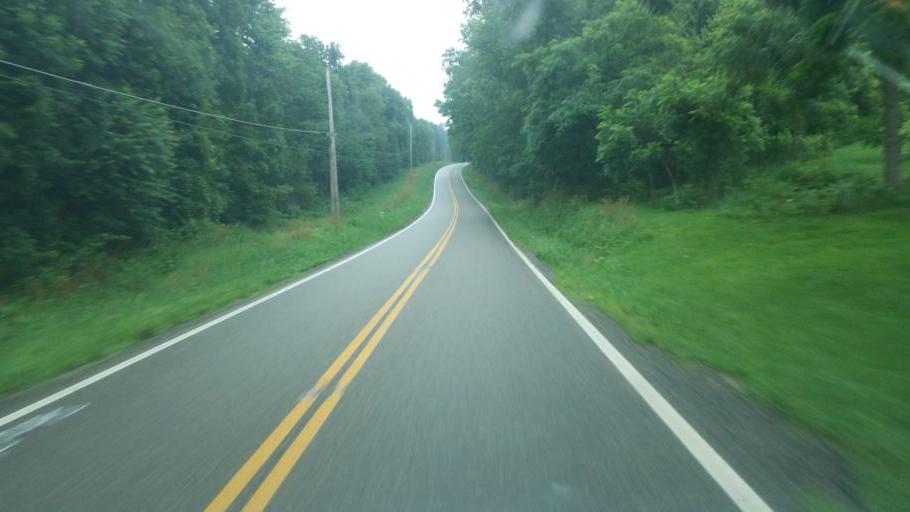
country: US
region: Ohio
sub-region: Tuscarawas County
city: Rockford
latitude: 40.4443
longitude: -81.1847
